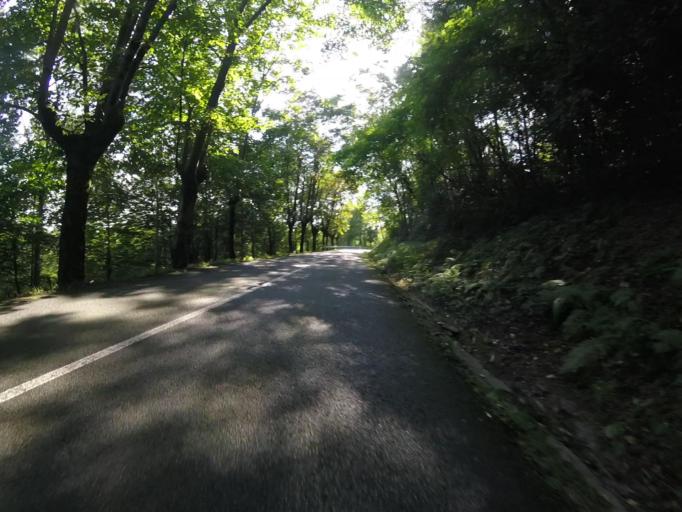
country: ES
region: Basque Country
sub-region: Provincia de Guipuzcoa
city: Irun
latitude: 43.3317
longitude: -1.7649
